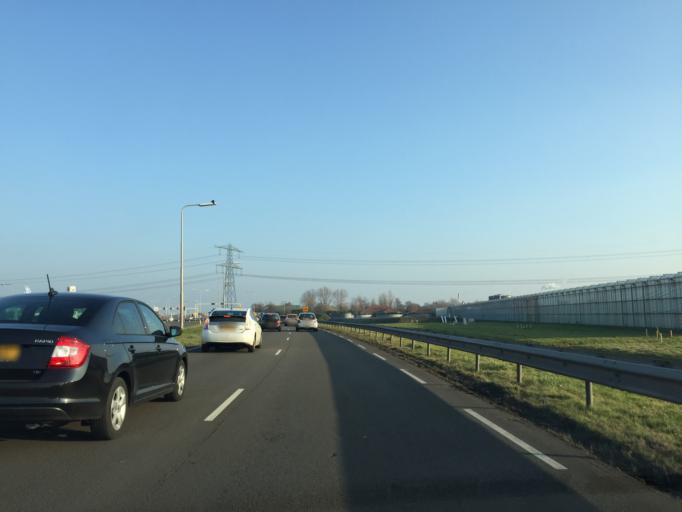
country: NL
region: South Holland
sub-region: Gemeente Westland
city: Kwintsheul
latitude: 52.0109
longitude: 4.2852
